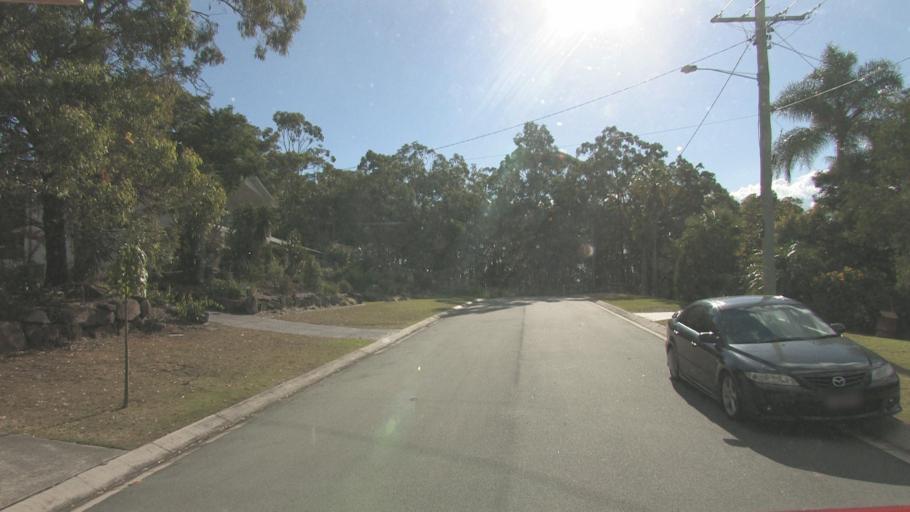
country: AU
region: Queensland
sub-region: Logan
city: Beenleigh
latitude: -27.6678
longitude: 153.2141
